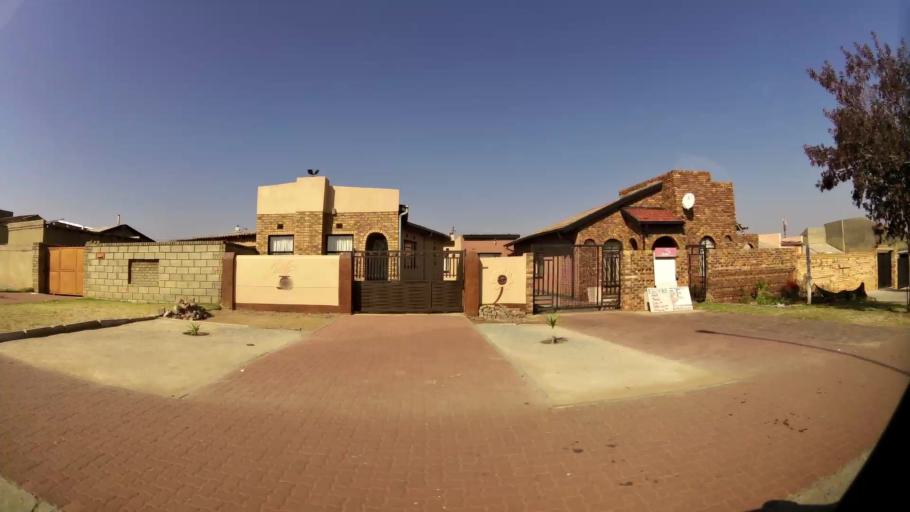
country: ZA
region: Gauteng
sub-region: City of Johannesburg Metropolitan Municipality
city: Soweto
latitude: -26.2431
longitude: 27.9424
